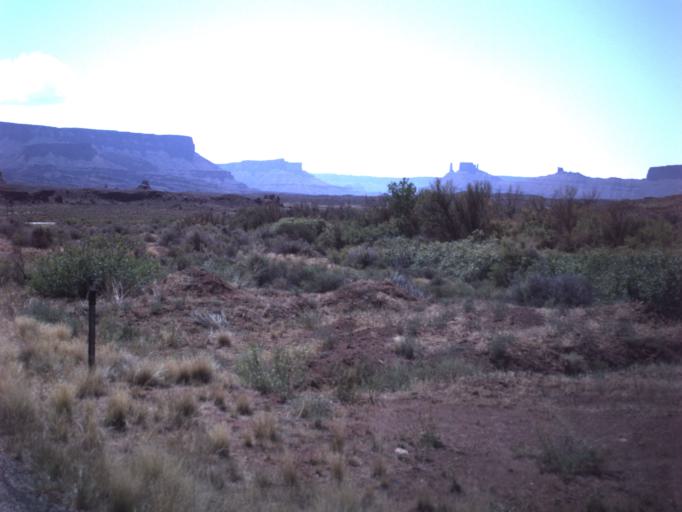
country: US
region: Utah
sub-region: Grand County
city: Moab
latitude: 38.7677
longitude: -109.3206
